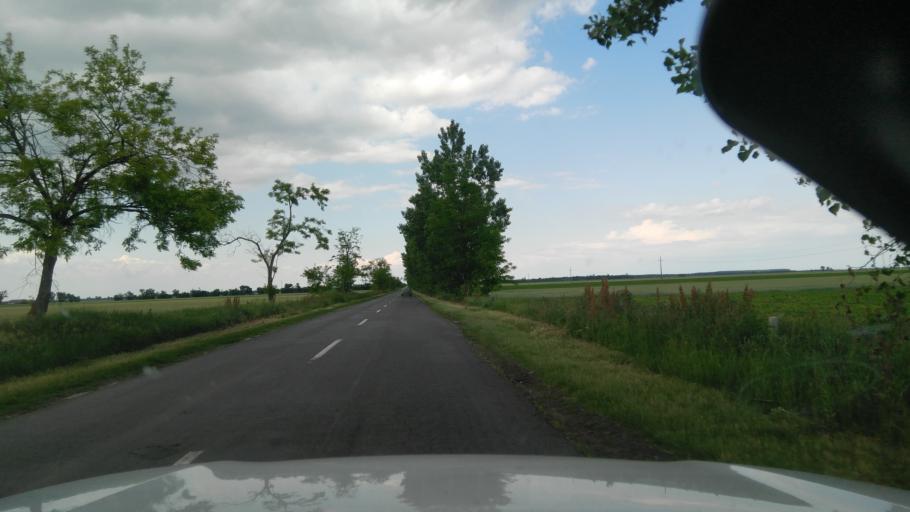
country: HU
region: Bekes
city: Magyarbanhegyes
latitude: 46.4573
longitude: 21.0020
